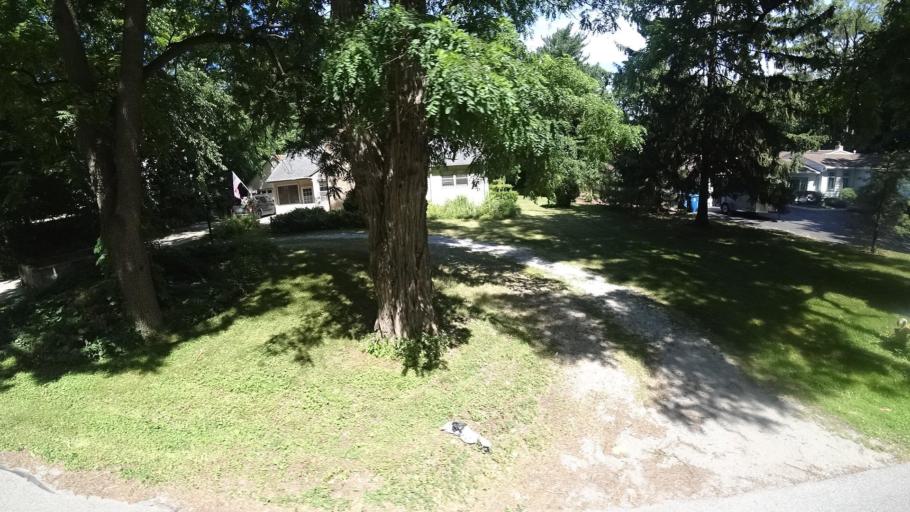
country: US
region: Indiana
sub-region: Porter County
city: Porter
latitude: 41.6280
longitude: -87.0673
